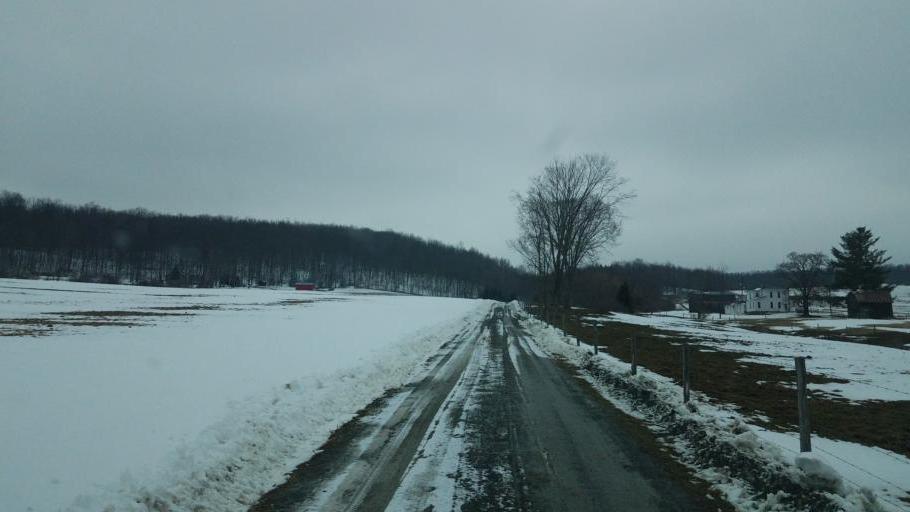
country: US
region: Pennsylvania
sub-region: Tioga County
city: Elkland
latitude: 42.0793
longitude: -77.4521
